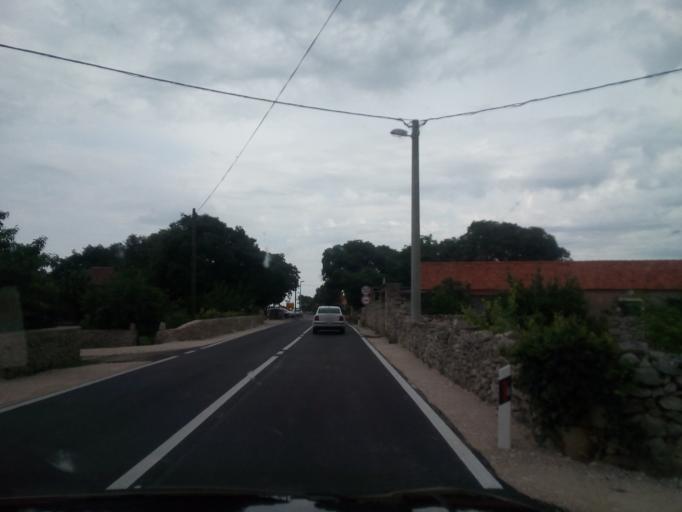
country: HR
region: Sibensko-Kniniska
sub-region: Grad Sibenik
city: Sibenik
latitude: 43.7823
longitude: 15.9663
